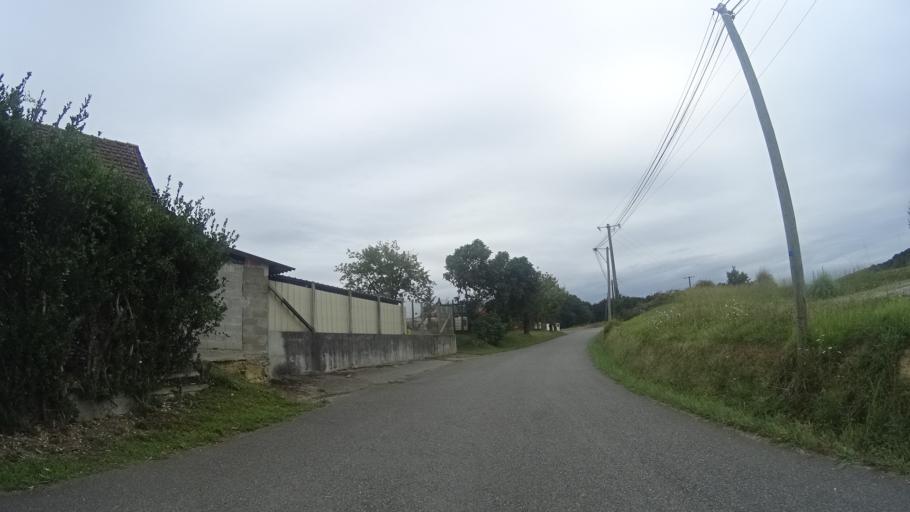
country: FR
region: Aquitaine
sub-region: Departement des Pyrenees-Atlantiques
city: Orthez
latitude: 43.4751
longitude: -0.7296
